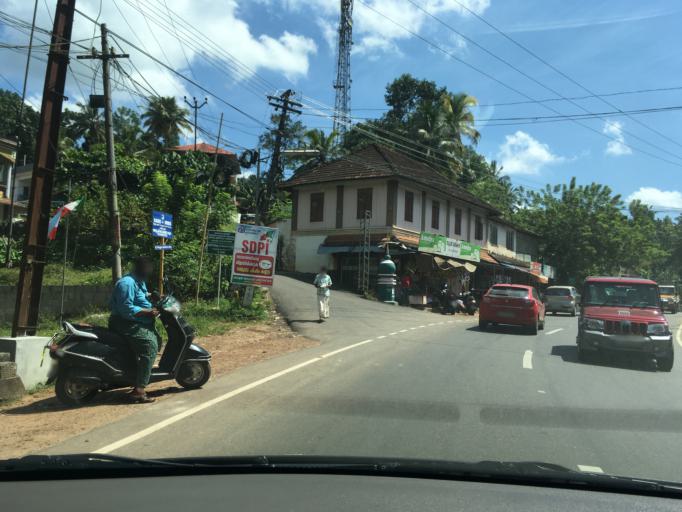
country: IN
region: Kerala
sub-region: Thiruvananthapuram
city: Nedumangad
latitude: 8.5747
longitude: 76.9967
